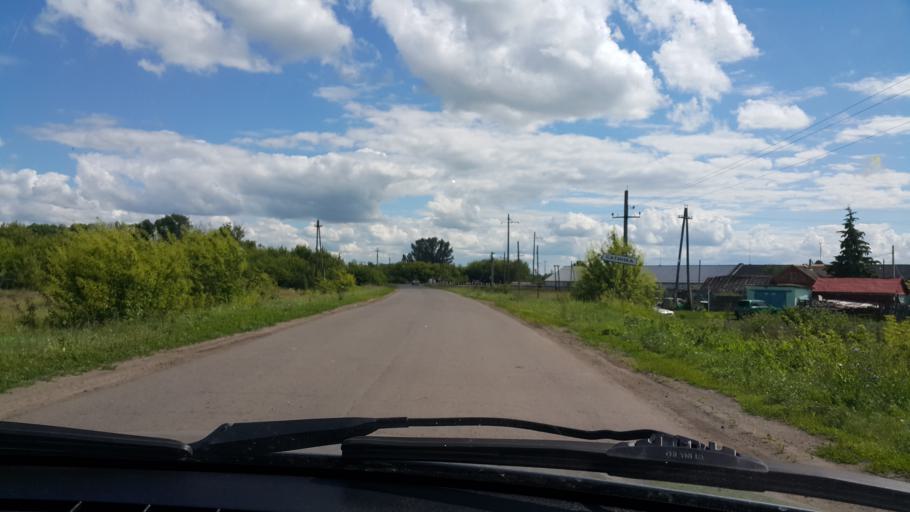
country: RU
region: Tambov
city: Satinka
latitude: 52.3846
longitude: 41.6633
